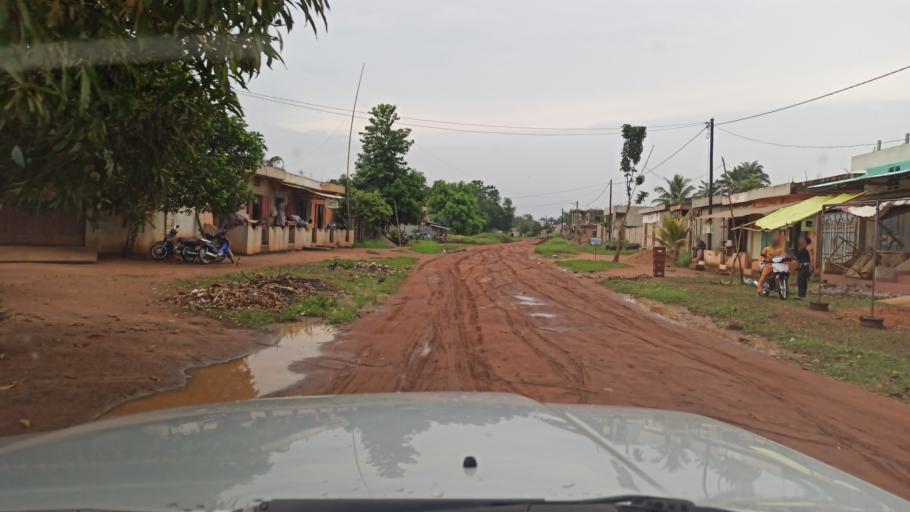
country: BJ
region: Queme
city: Porto-Novo
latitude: 6.4817
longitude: 2.6724
